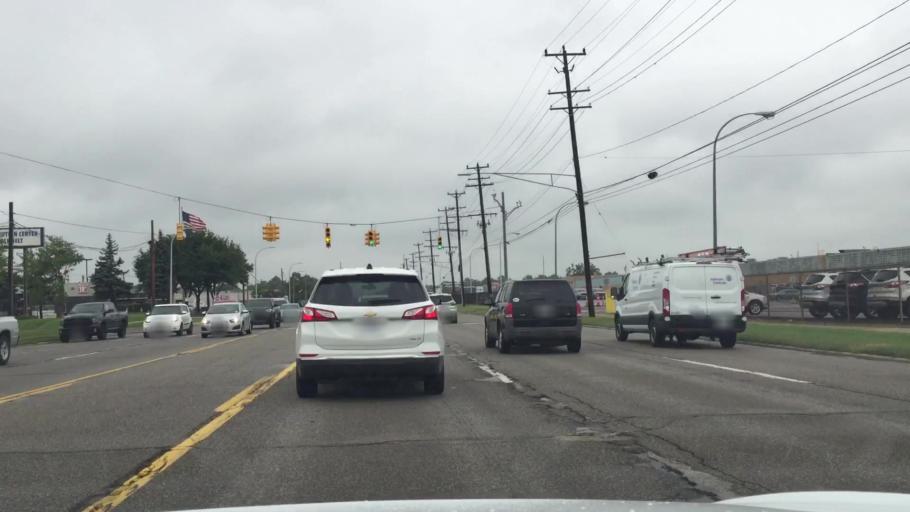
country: US
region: Michigan
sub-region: Wayne County
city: Livonia
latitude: 42.3738
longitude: -83.3333
